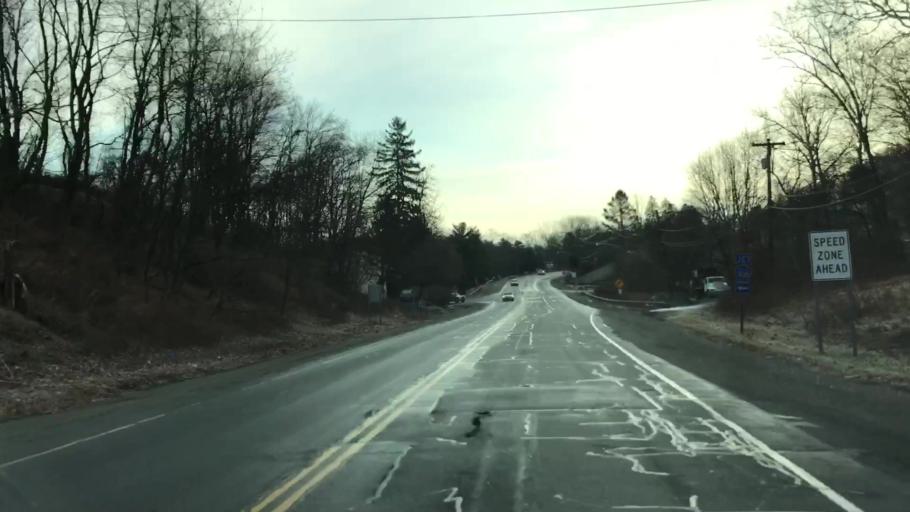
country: US
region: New York
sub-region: Rockland County
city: Stony Point
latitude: 41.2350
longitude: -74.0113
